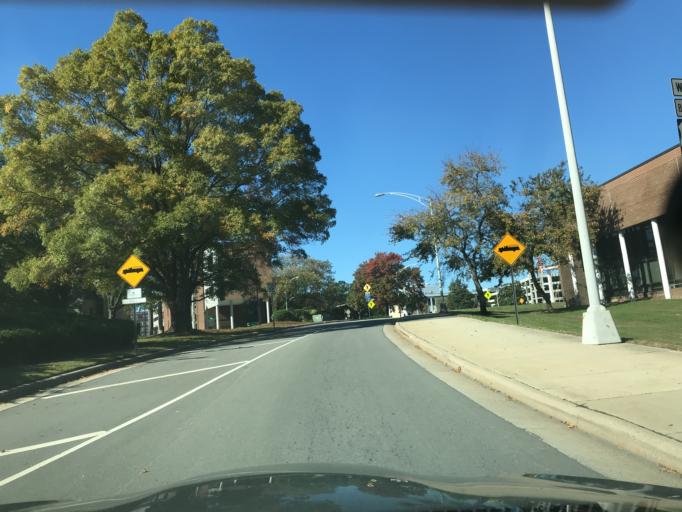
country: US
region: North Carolina
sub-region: Durham County
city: Durham
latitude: 35.9956
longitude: -78.8970
